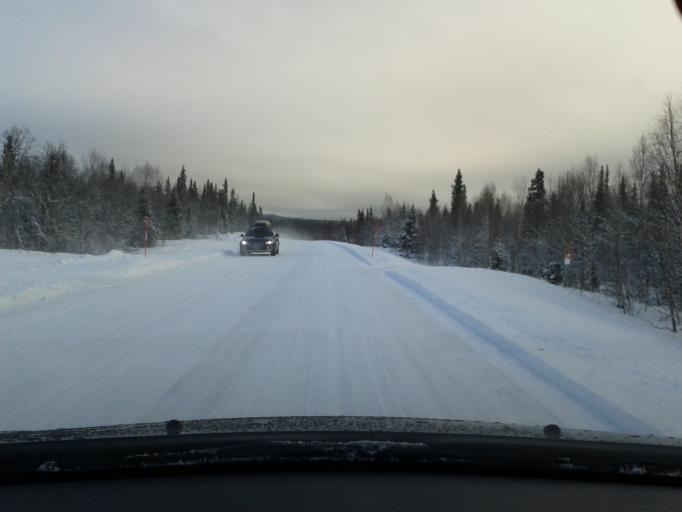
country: SE
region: Vaesterbotten
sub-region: Vilhelmina Kommun
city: Sjoberg
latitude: 65.2570
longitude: 15.7071
